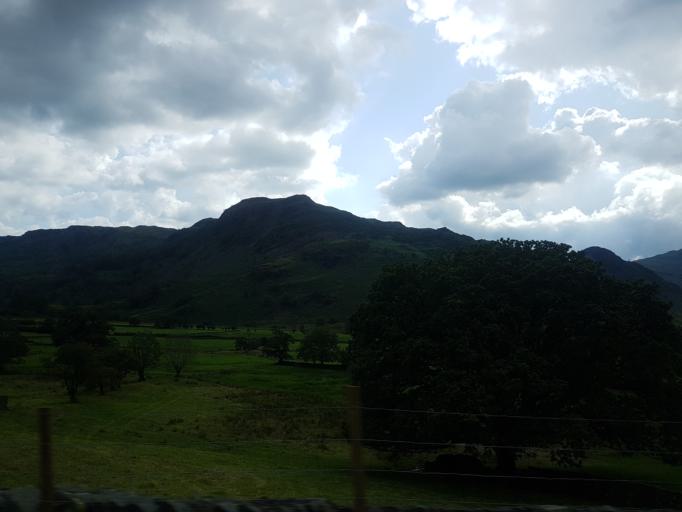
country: GB
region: England
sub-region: Cumbria
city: Ambleside
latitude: 54.4504
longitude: -3.0714
